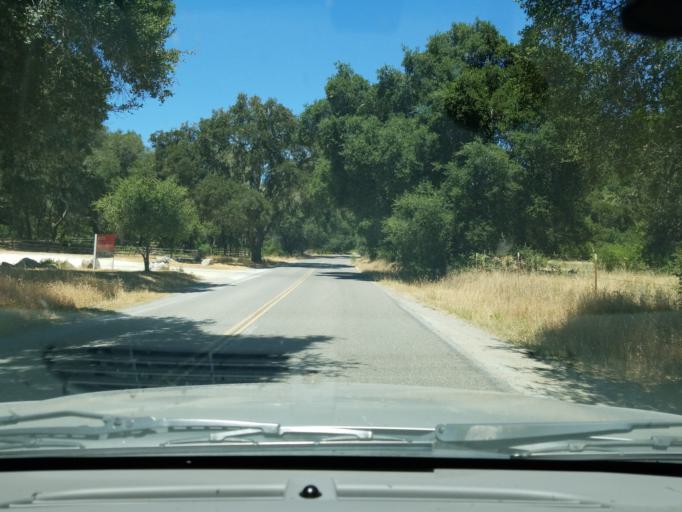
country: US
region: California
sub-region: Monterey County
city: Chualar
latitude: 36.4159
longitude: -121.6041
